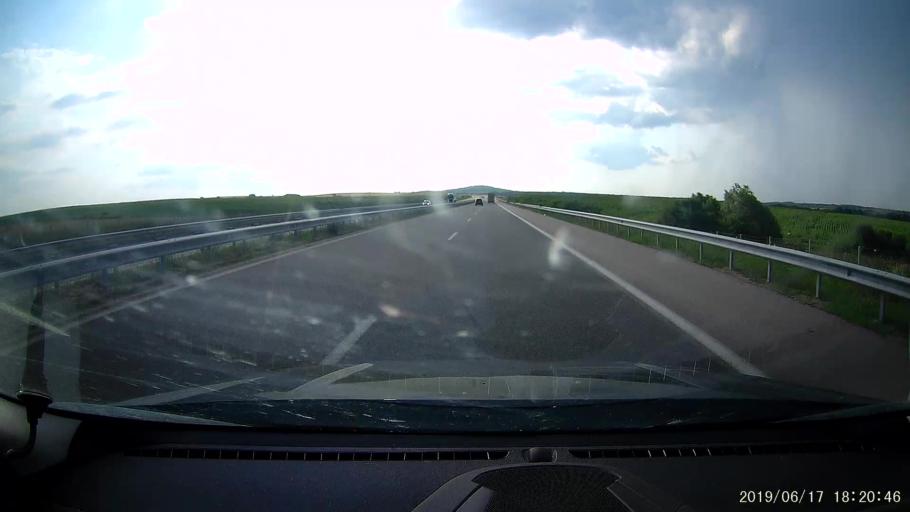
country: BG
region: Khaskovo
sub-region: Obshtina Simeonovgrad
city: Simeonovgrad
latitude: 41.9641
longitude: 25.8030
